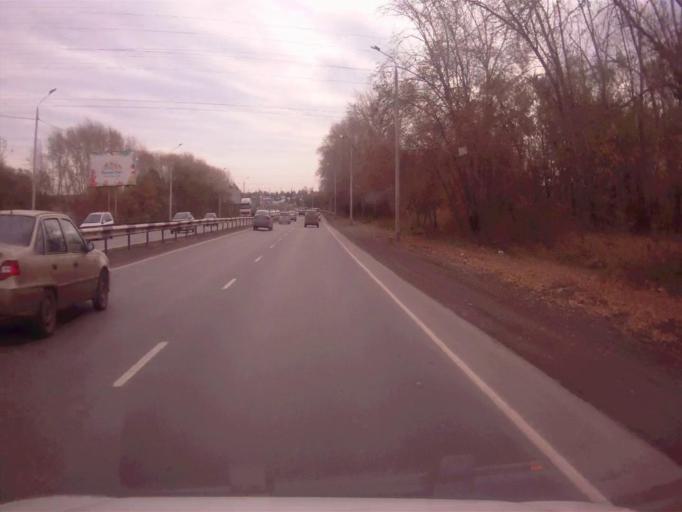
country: RU
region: Chelyabinsk
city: Novosineglazovskiy
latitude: 55.0504
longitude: 61.4130
